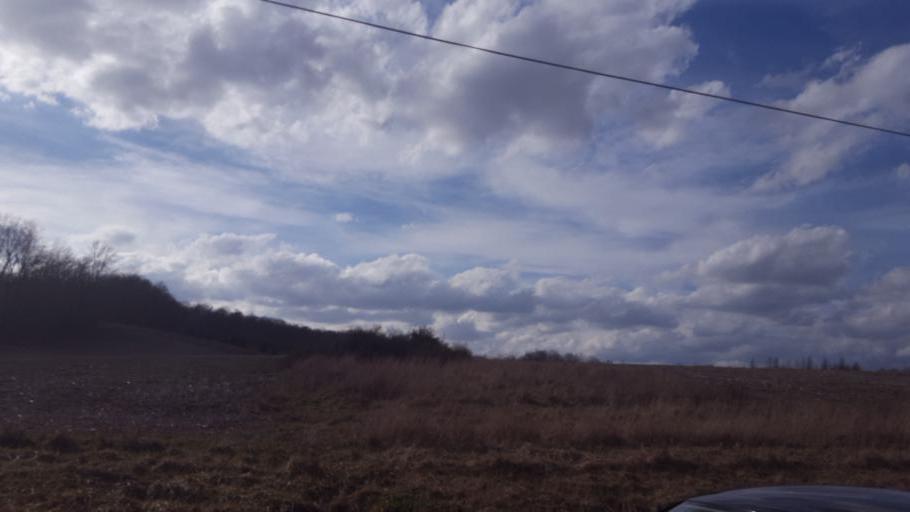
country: US
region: Ohio
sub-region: Ashland County
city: Loudonville
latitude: 40.5583
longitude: -82.3489
